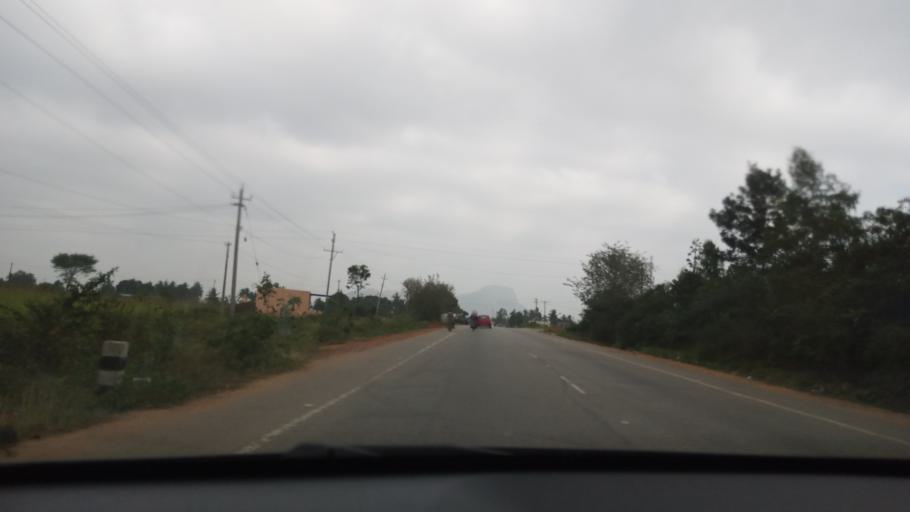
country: IN
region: Karnataka
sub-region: Chikkaballapur
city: Chintamani
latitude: 13.3018
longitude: 77.9714
